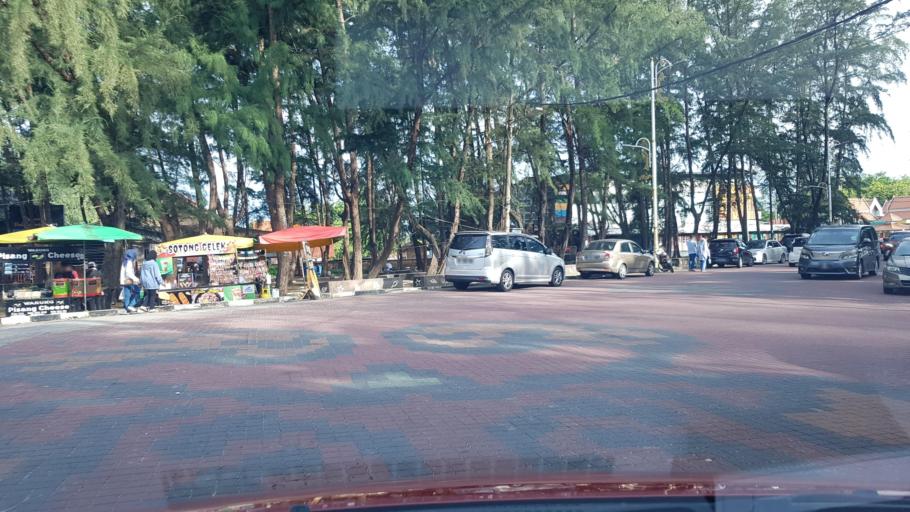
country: MY
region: Terengganu
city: Kuala Terengganu
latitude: 5.3223
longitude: 103.1548
